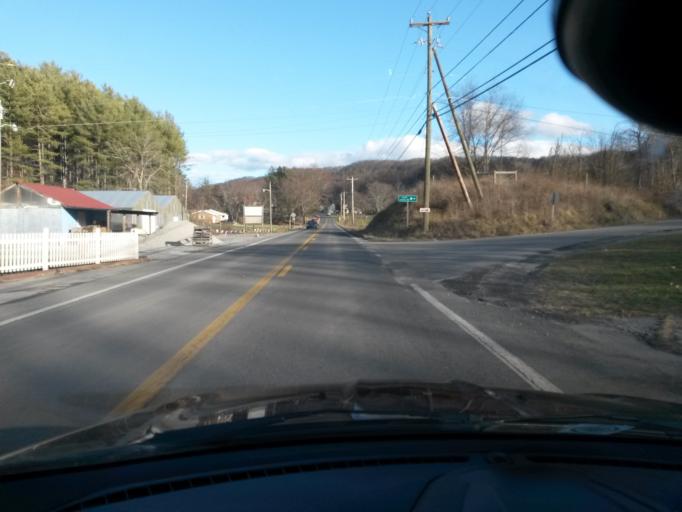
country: US
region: Virginia
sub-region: Giles County
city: Narrows
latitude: 37.4011
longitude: -80.7700
